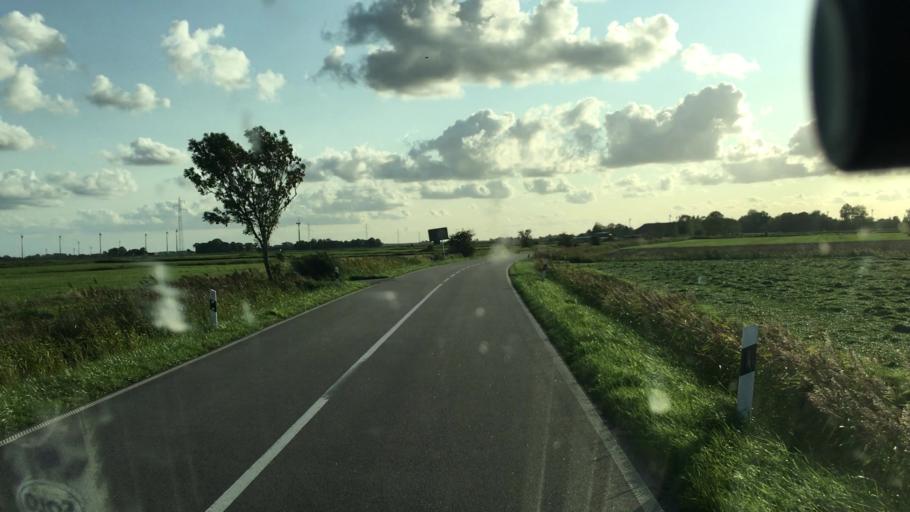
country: DE
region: Lower Saxony
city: Jever
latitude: 53.6381
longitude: 7.8605
